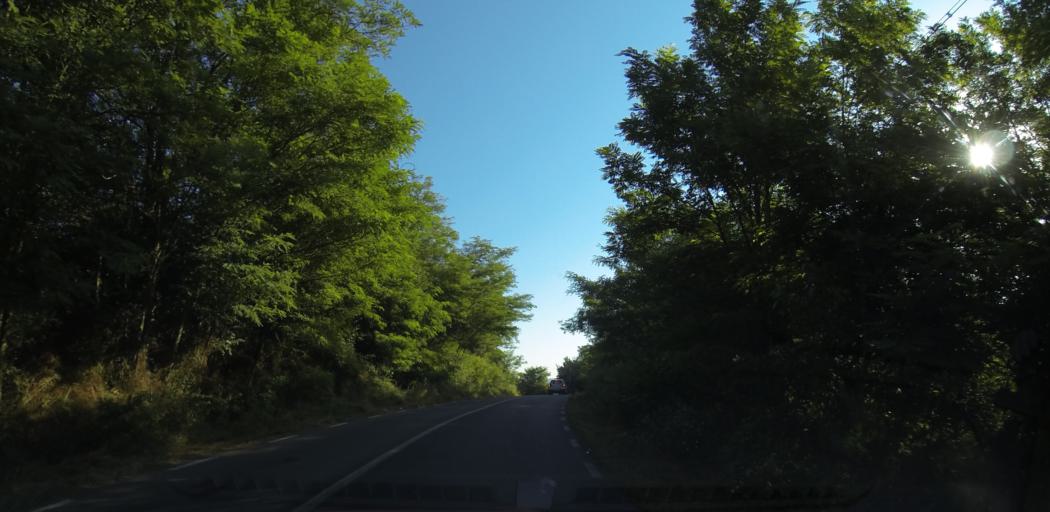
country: RO
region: Valcea
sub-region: Comuna Lacusteni
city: Lacusteni
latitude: 44.7173
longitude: 23.9023
